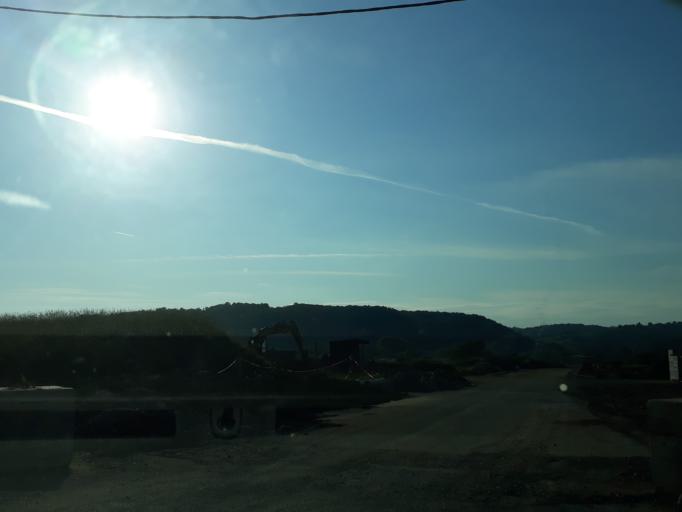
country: FR
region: Limousin
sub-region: Departement de la Correze
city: Saint-Pantaleon-de-Larche
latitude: 45.1538
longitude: 1.4685
